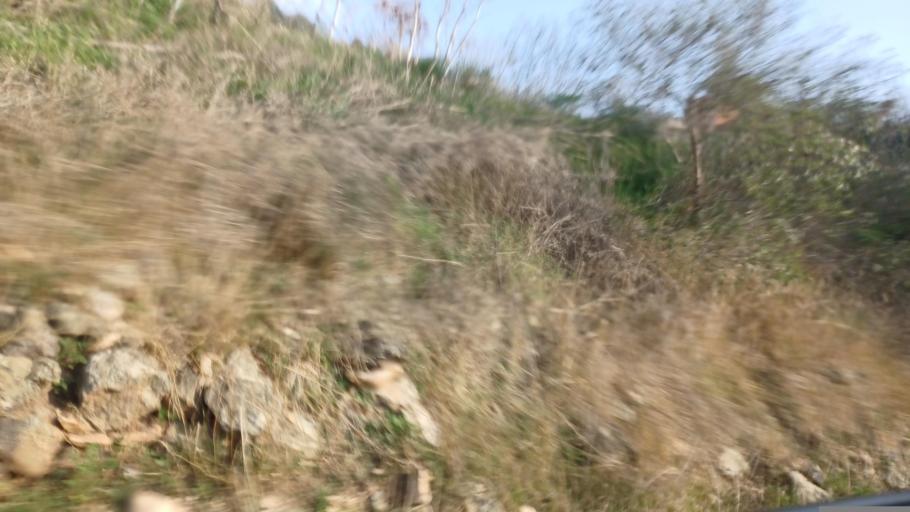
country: CY
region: Pafos
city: Mesogi
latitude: 34.7902
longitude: 32.4926
